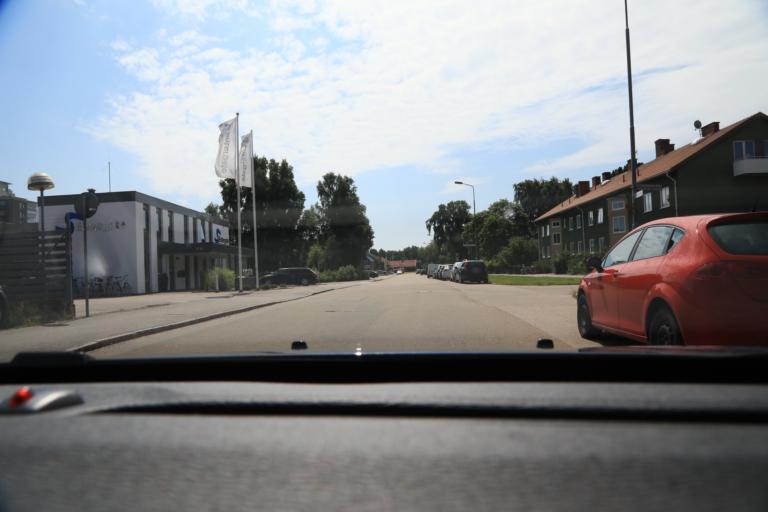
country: SE
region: Halland
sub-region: Halmstads Kommun
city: Halmstad
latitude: 56.6660
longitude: 12.8539
